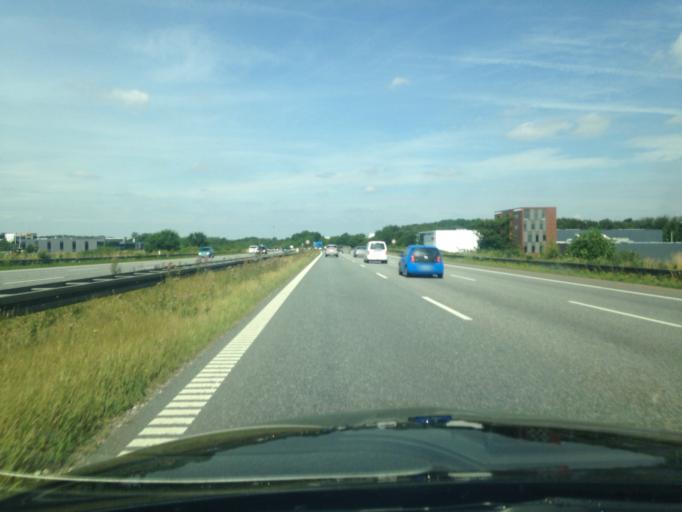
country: DK
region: South Denmark
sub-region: Fredericia Kommune
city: Snoghoj
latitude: 55.5264
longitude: 9.7263
